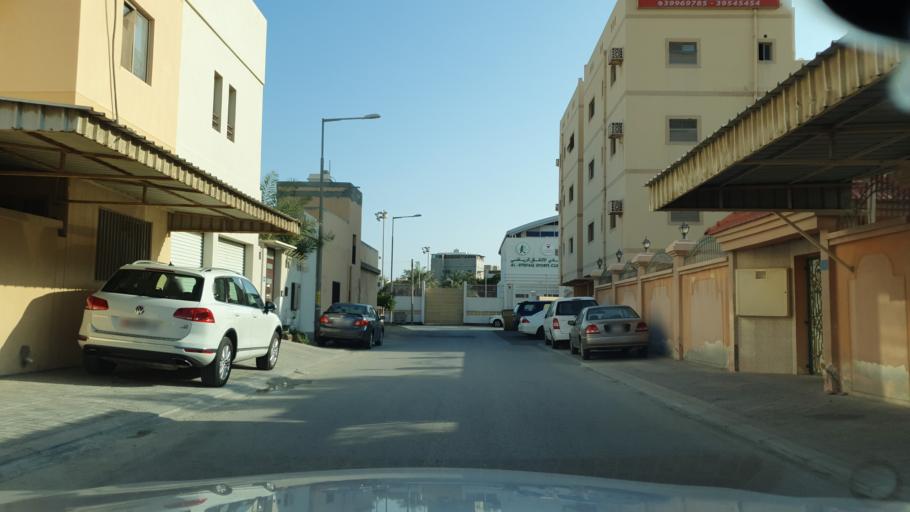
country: BH
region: Manama
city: Jidd Hafs
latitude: 26.2222
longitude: 50.4621
